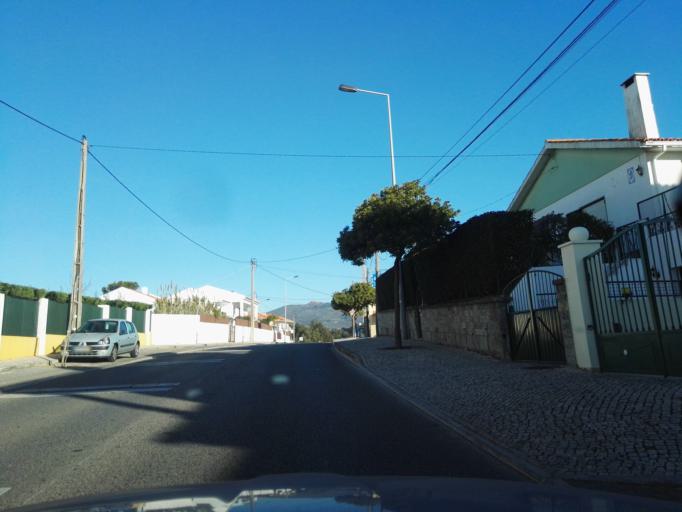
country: PT
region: Lisbon
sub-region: Cascais
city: Alcabideche
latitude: 38.7296
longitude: -9.4447
